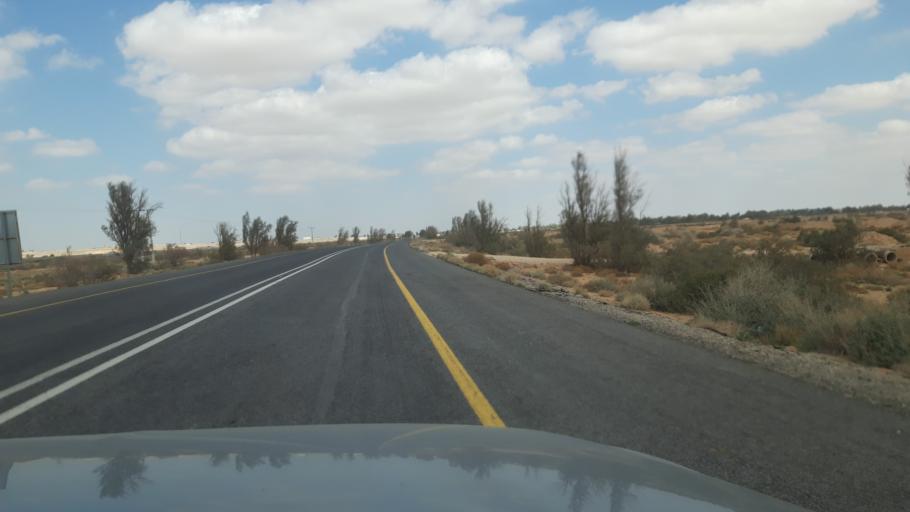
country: JO
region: Amman
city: Al Azraq ash Shamali
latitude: 31.8106
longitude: 36.7989
